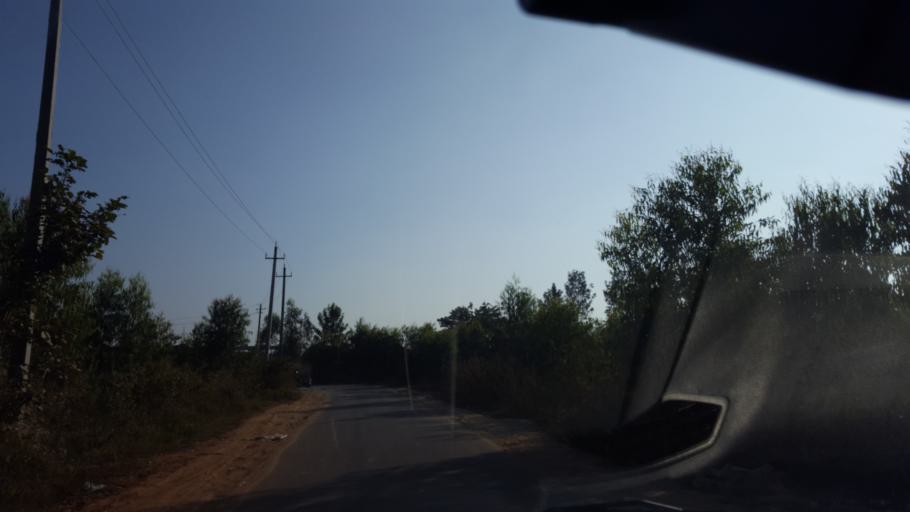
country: IN
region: Karnataka
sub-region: Bangalore Rural
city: Hoskote
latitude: 12.9240
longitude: 77.7563
